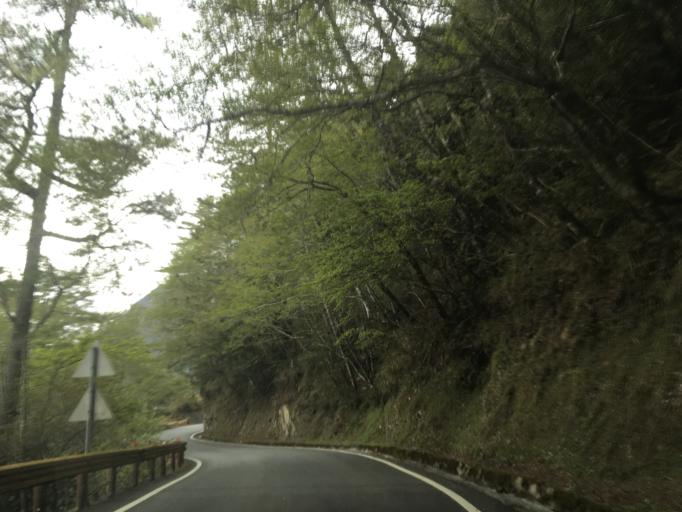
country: TW
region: Taiwan
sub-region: Hualien
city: Hualian
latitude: 24.1732
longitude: 121.3790
